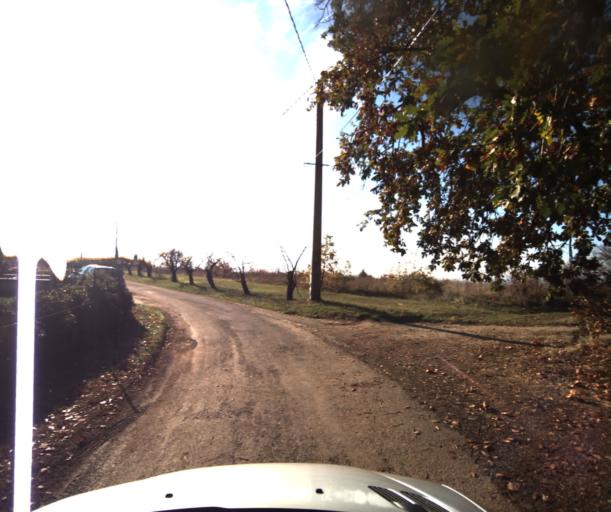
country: FR
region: Midi-Pyrenees
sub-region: Departement du Tarn-et-Garonne
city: Lafrancaise
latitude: 44.1080
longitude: 1.2863
